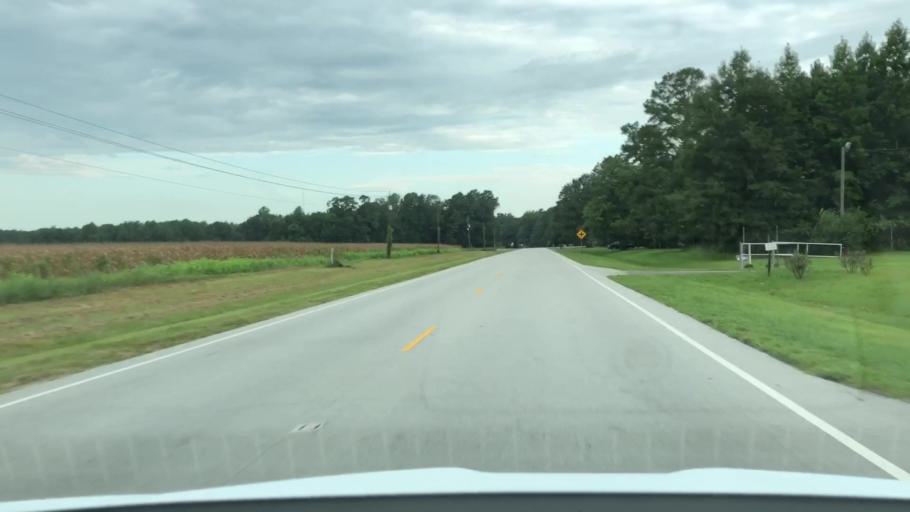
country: US
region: North Carolina
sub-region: Jones County
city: Trenton
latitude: 35.0301
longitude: -77.3130
